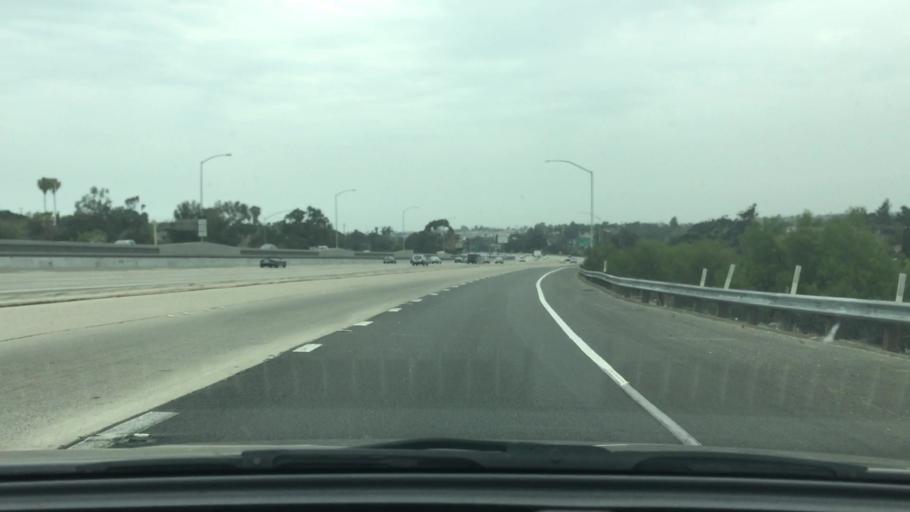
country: US
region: California
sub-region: San Diego County
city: Chula Vista
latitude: 32.6418
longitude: -117.0560
